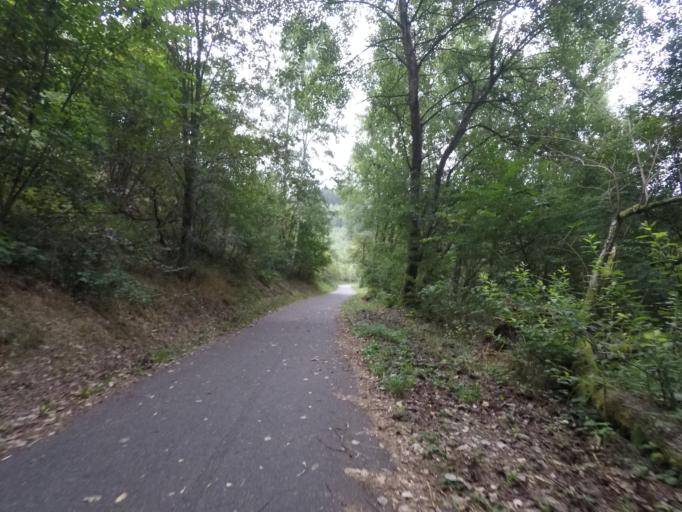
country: BE
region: Wallonia
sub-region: Province du Luxembourg
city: Martelange
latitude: 49.8438
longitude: 5.7260
